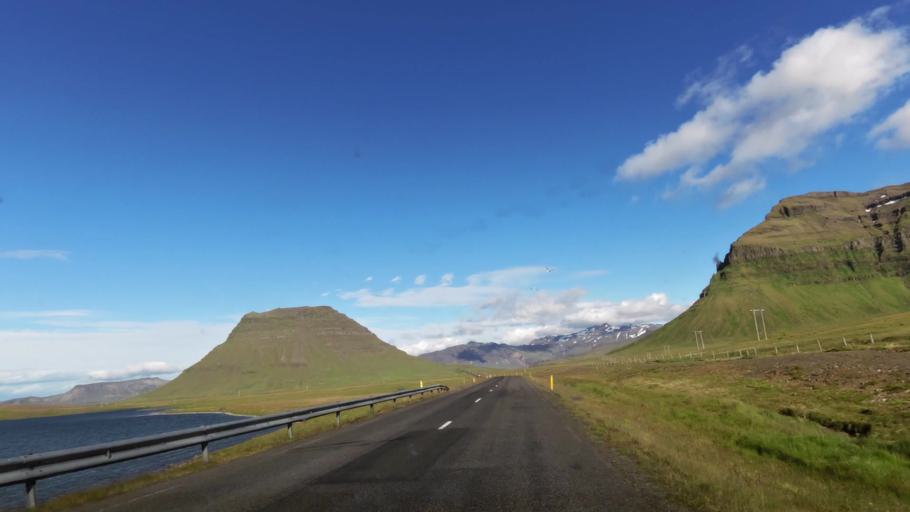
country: IS
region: West
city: Olafsvik
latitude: 64.9426
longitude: -23.3805
